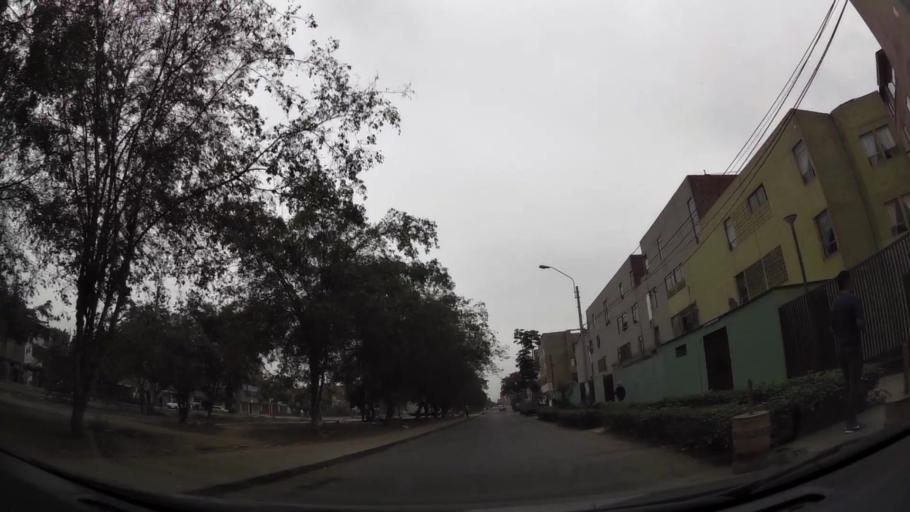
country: PE
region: Lima
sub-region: Lima
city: Independencia
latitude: -11.9668
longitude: -77.0612
